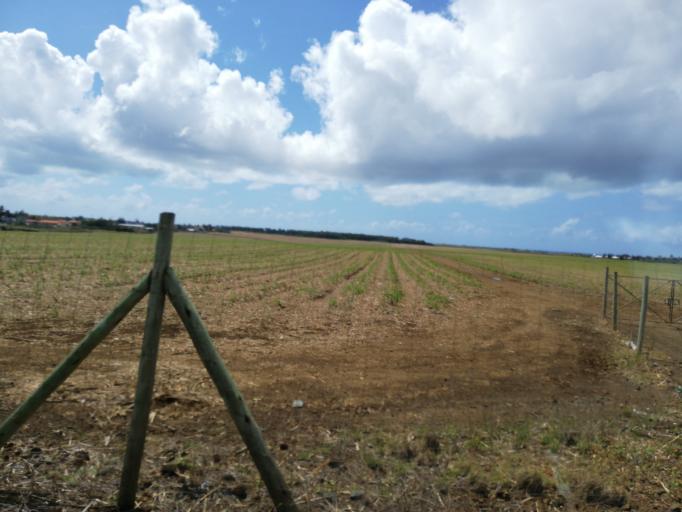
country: MU
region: Riviere du Rempart
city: Esperance Trebuchet
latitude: -20.0693
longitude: 57.6380
